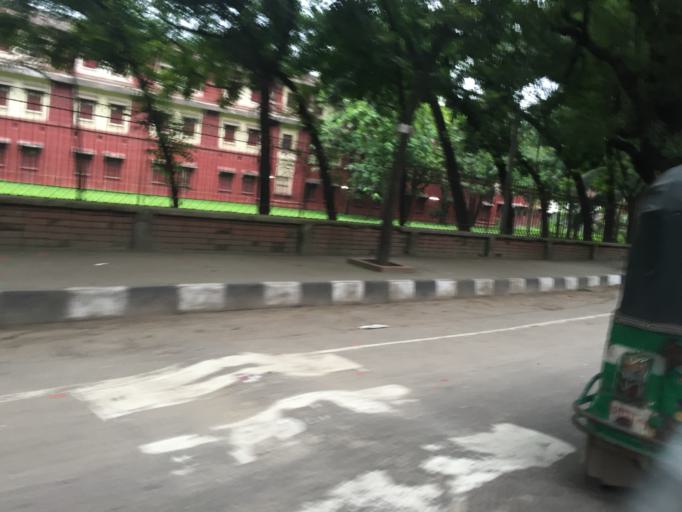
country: BD
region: Dhaka
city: Paltan
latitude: 23.7260
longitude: 90.4045
